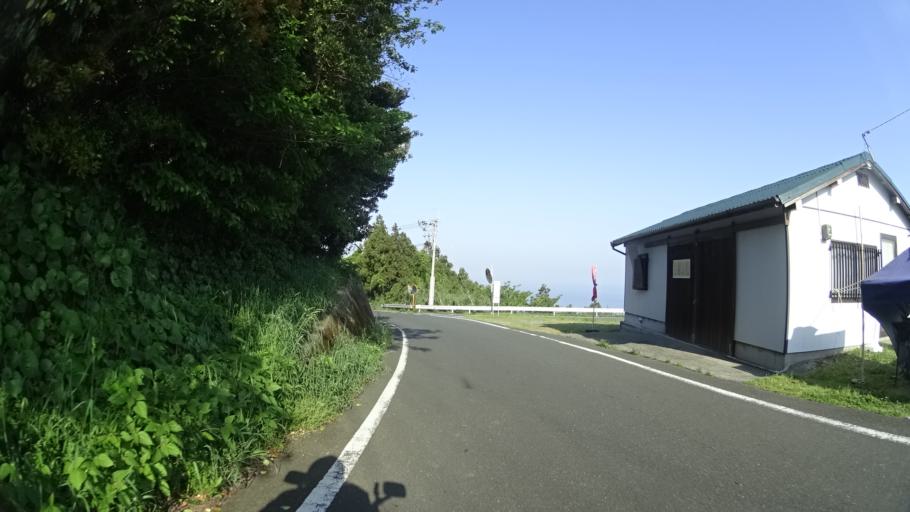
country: JP
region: Ehime
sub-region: Nishiuwa-gun
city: Ikata-cho
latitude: 33.3823
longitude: 132.0753
